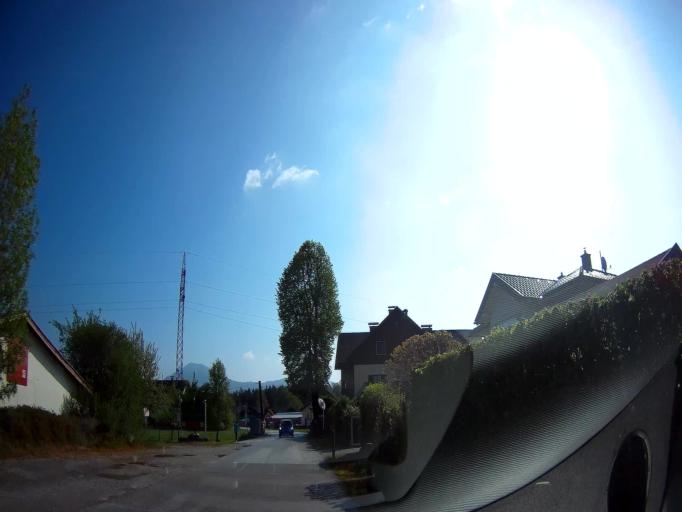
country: AT
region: Salzburg
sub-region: Politischer Bezirk Salzburg-Umgebung
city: Grodig
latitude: 47.7539
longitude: 13.0342
